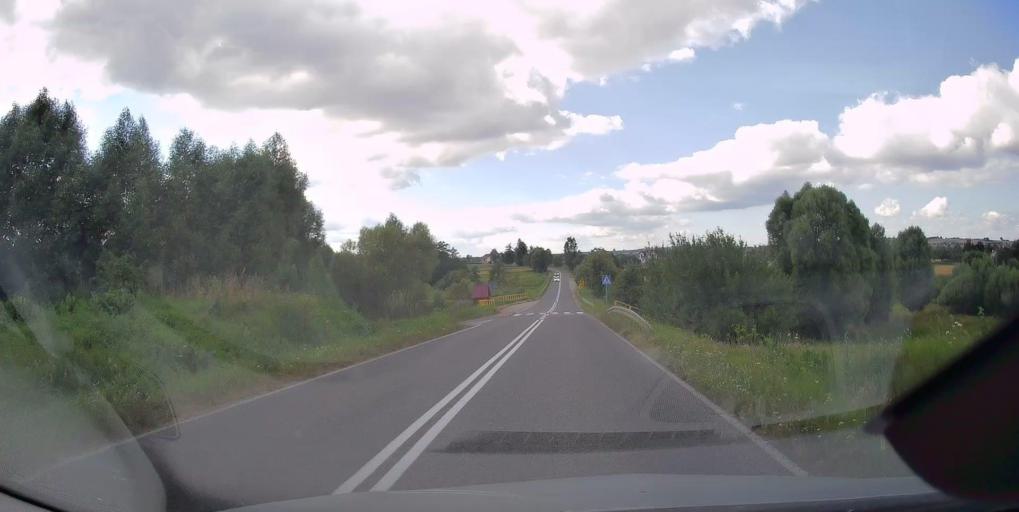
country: PL
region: Swietokrzyskie
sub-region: Powiat kielecki
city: Nowa Slupia
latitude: 50.8894
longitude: 21.0429
